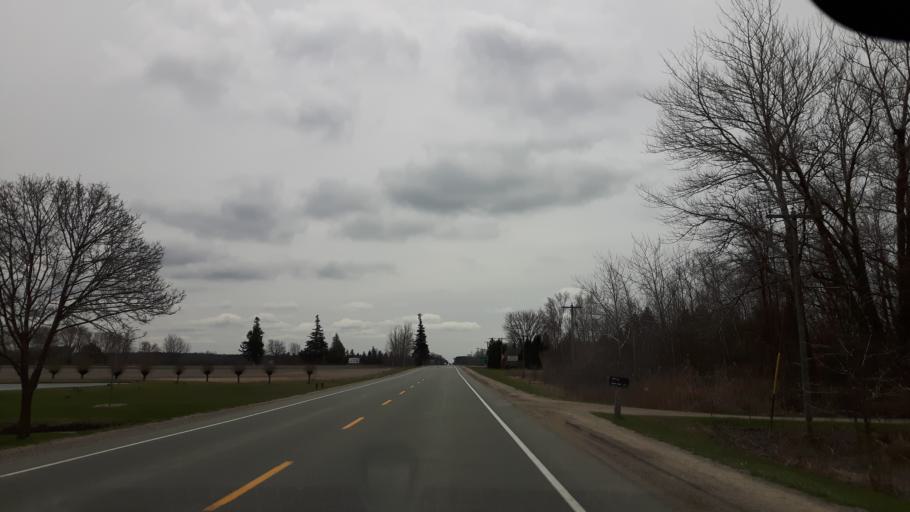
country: CA
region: Ontario
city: Goderich
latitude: 43.7006
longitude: -81.7057
